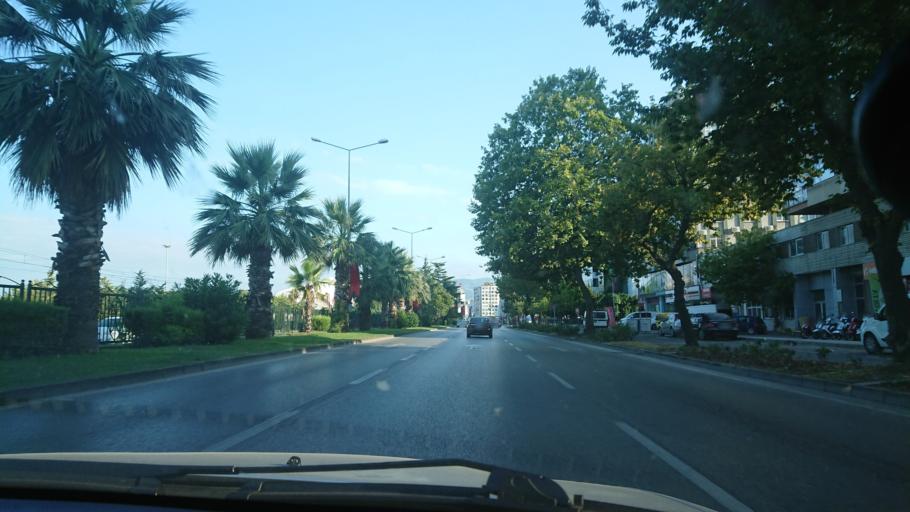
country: TR
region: Samsun
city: Samsun
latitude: 41.2982
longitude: 36.3323
